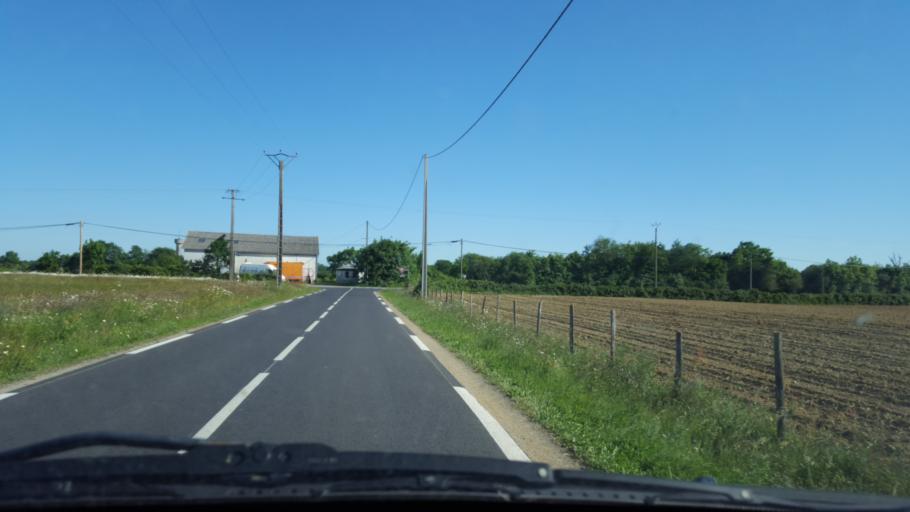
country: FR
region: Pays de la Loire
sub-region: Departement de la Loire-Atlantique
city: Saint-Philbert-de-Grand-Lieu
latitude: 47.0271
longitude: -1.6780
